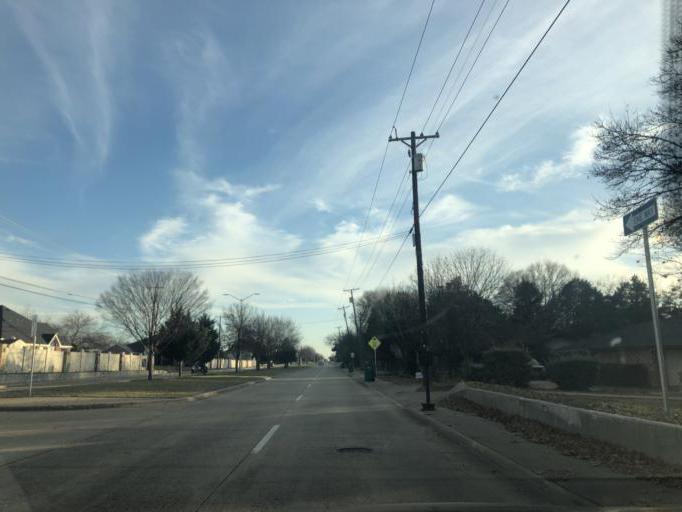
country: US
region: Texas
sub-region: Dallas County
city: Cedar Hill
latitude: 32.6006
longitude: -96.9255
